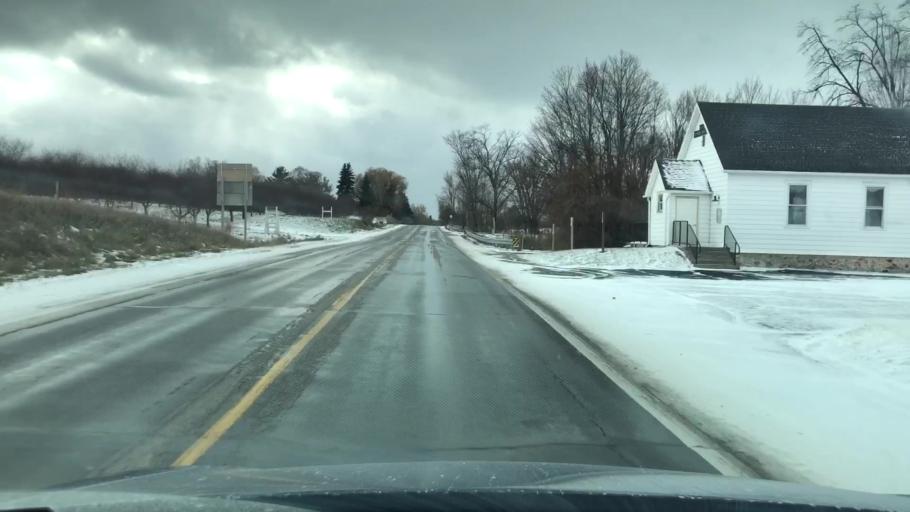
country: US
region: Michigan
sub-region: Antrim County
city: Elk Rapids
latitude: 44.8805
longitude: -85.5154
